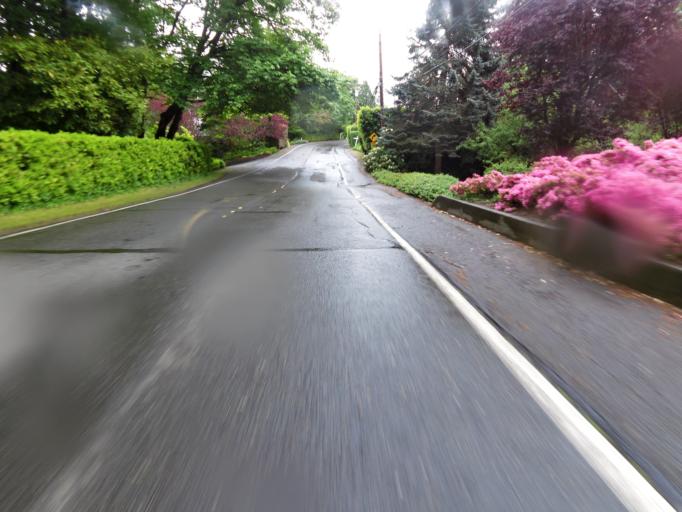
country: US
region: Washington
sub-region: King County
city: Medina
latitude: 47.5948
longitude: -122.2446
